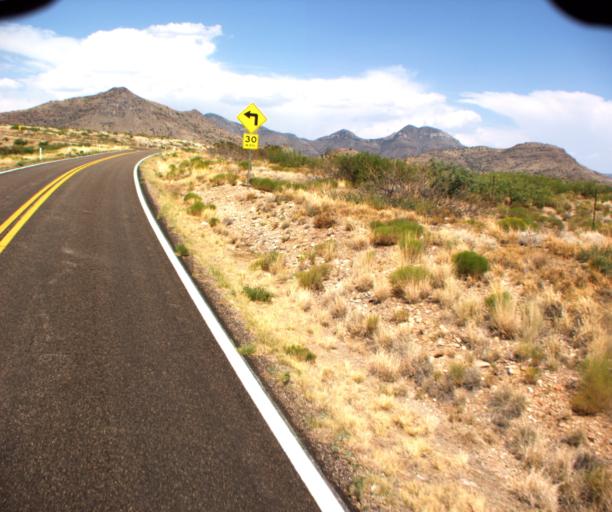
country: US
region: Arizona
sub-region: Greenlee County
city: Clifton
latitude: 33.0043
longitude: -109.1634
